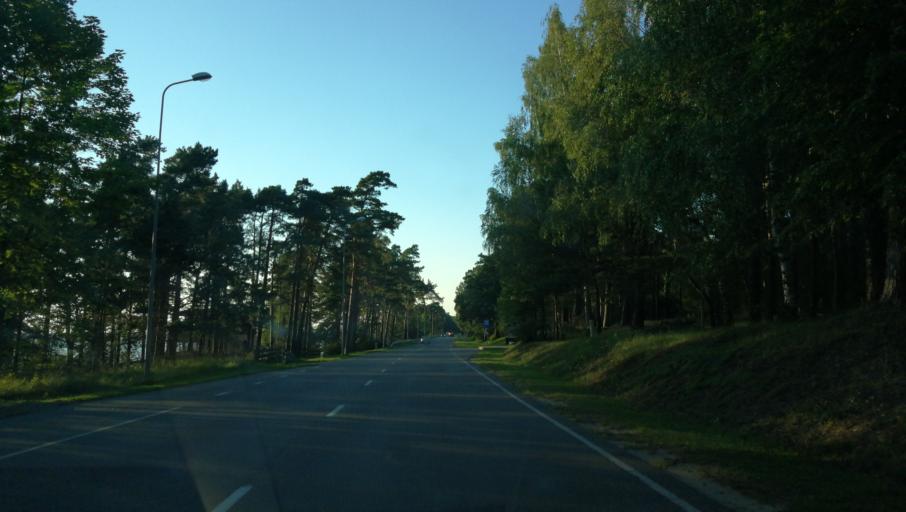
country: LV
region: Saulkrastu
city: Saulkrasti
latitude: 57.2852
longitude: 24.4140
